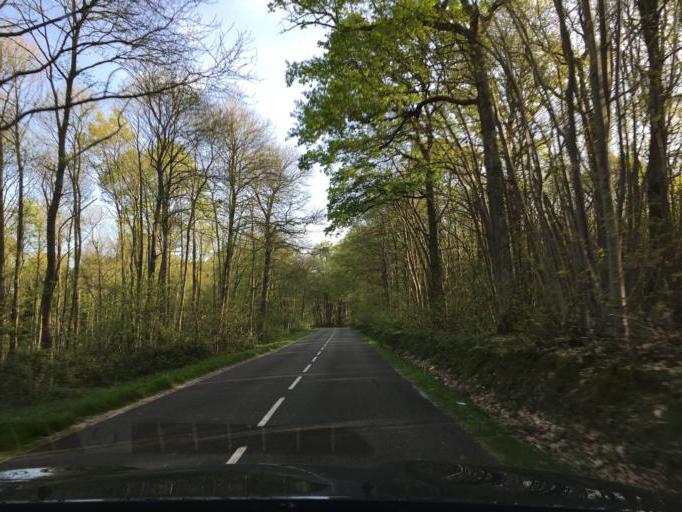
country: FR
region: Ile-de-France
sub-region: Departement des Yvelines
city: Conde-sur-Vesgre
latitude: 48.7014
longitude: 1.6599
